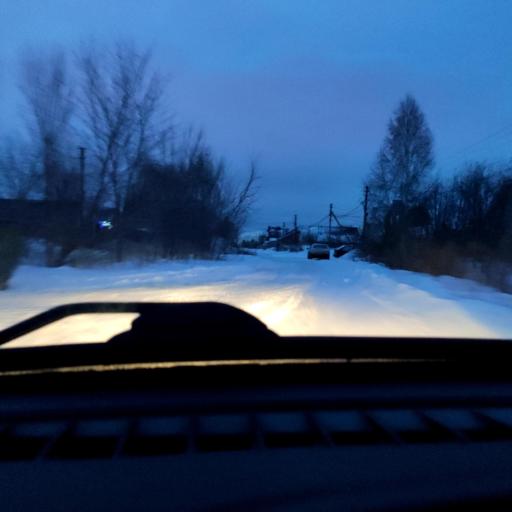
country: RU
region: Samara
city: Tol'yatti
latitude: 53.5538
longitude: 49.3730
